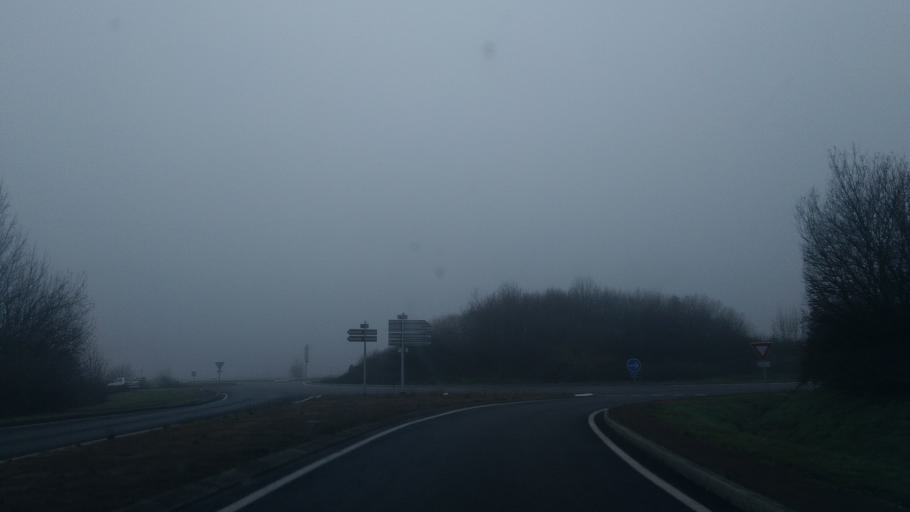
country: FR
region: Pays de la Loire
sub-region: Departement de la Vendee
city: Soullans
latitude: 46.8325
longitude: -1.9195
